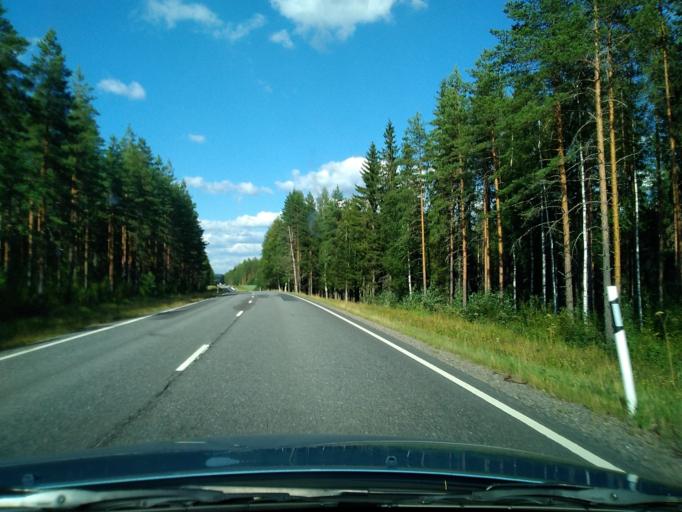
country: FI
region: Pirkanmaa
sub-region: Ylae-Pirkanmaa
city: Maenttae
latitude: 61.9623
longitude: 24.5908
